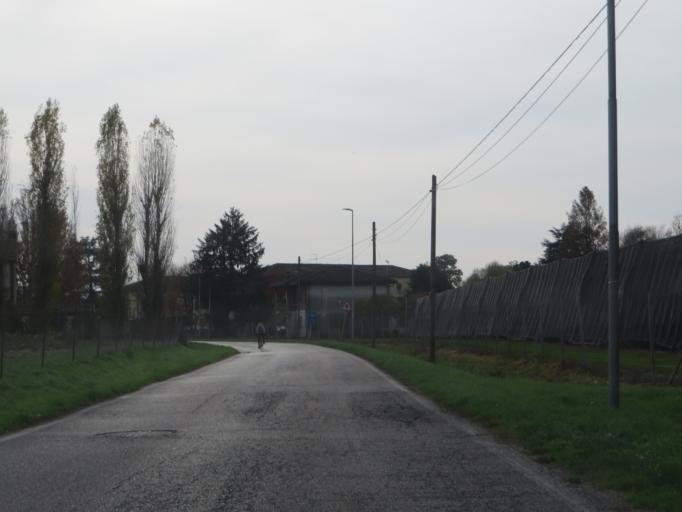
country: IT
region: Veneto
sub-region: Provincia di Verona
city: San Pietro di Morubio
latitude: 45.2502
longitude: 11.2331
